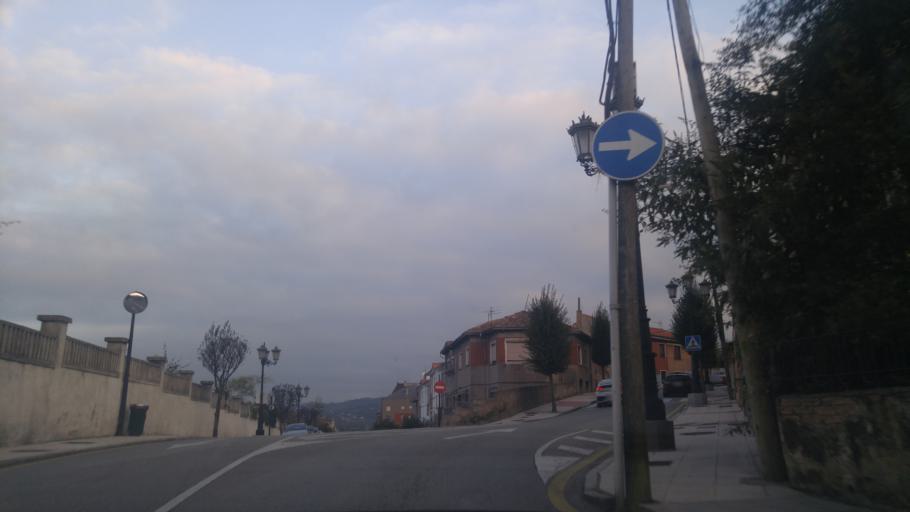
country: ES
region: Asturias
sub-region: Province of Asturias
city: Oviedo
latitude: 43.3727
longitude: -5.8576
